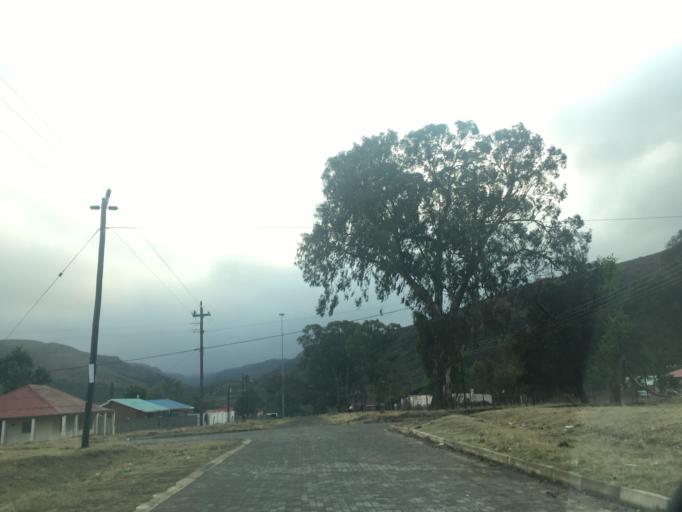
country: ZA
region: Eastern Cape
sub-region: Chris Hani District Municipality
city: Cala
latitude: -31.5236
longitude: 27.6991
